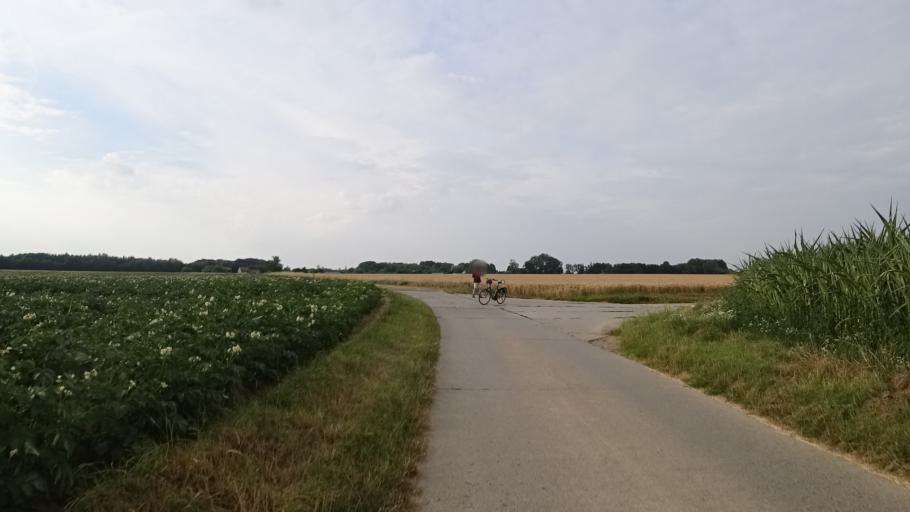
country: BE
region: Wallonia
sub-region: Province du Brabant Wallon
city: Perwez
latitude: 50.5755
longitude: 4.8282
